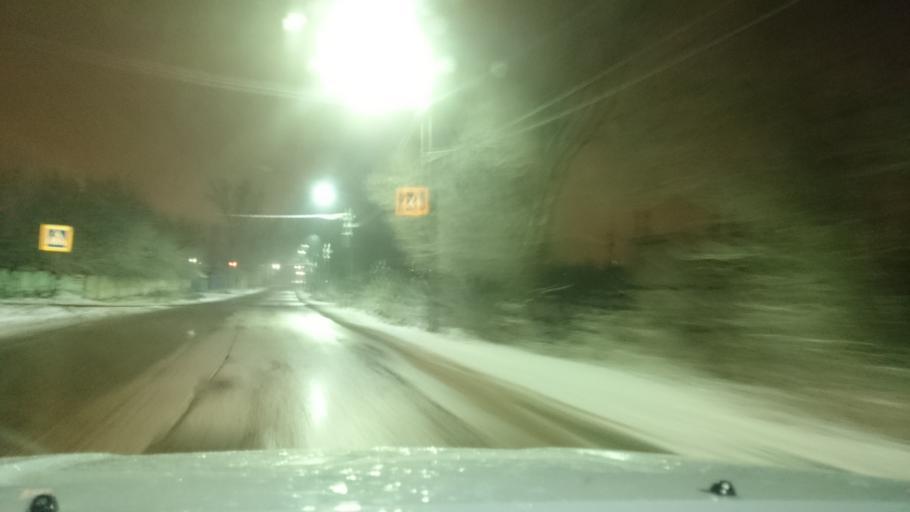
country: RU
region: Tula
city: Tula
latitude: 54.2223
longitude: 37.5899
